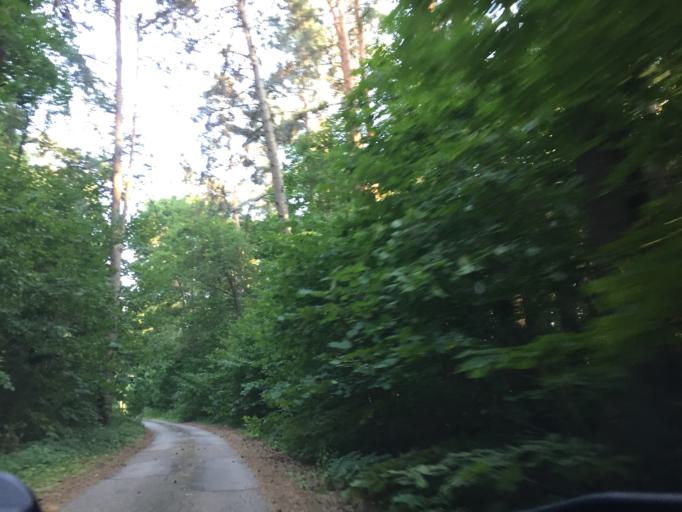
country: LV
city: Tervete
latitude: 56.4725
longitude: 23.3707
